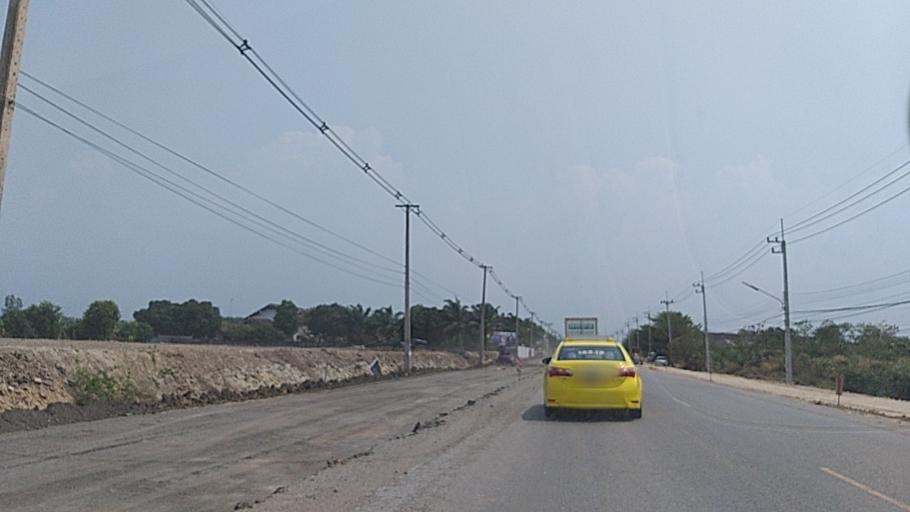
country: TH
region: Chon Buri
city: Phanat Nikhom
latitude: 13.4330
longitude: 101.1814
